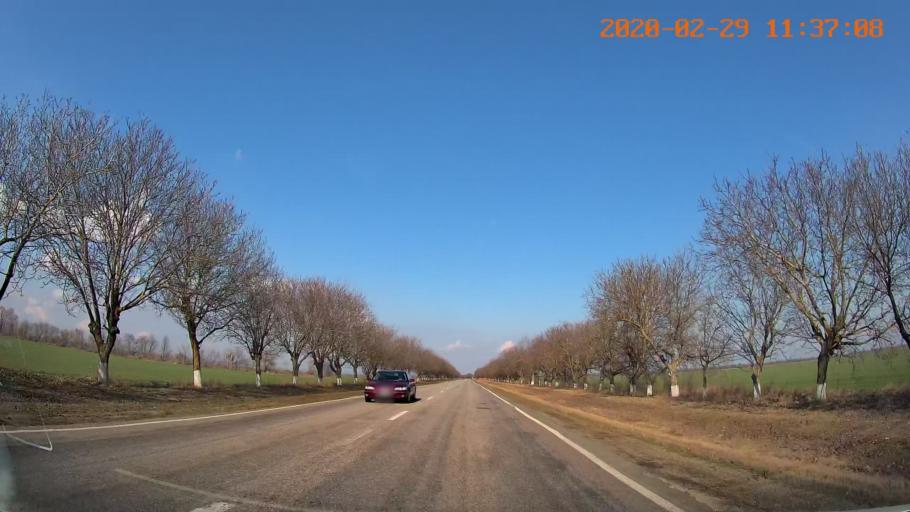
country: MD
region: Rezina
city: Saharna
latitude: 47.6072
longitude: 29.0487
